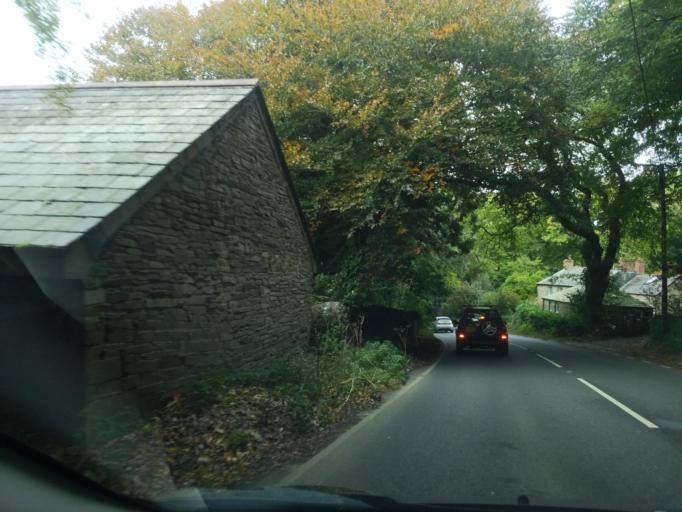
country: GB
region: England
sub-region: Cornwall
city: Bodmin
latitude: 50.4995
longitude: -4.7753
